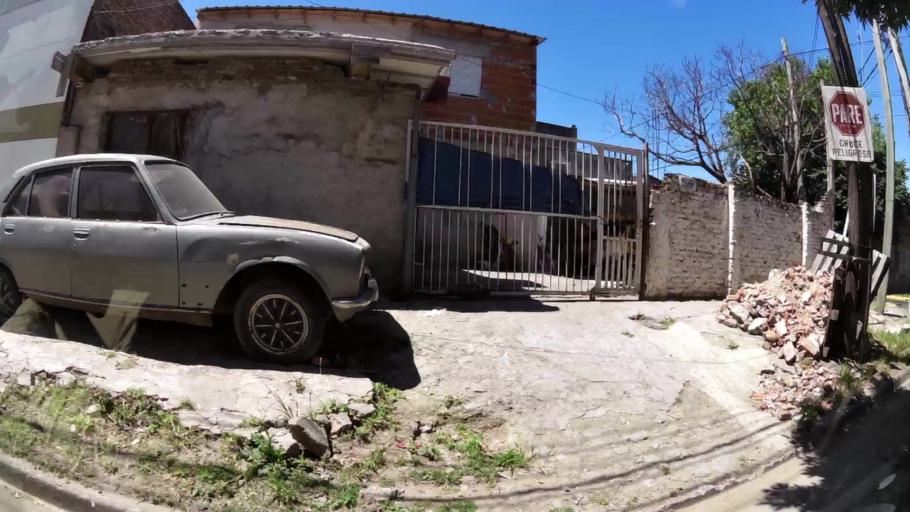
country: AR
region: Buenos Aires
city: Caseros
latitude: -34.5822
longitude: -58.5574
